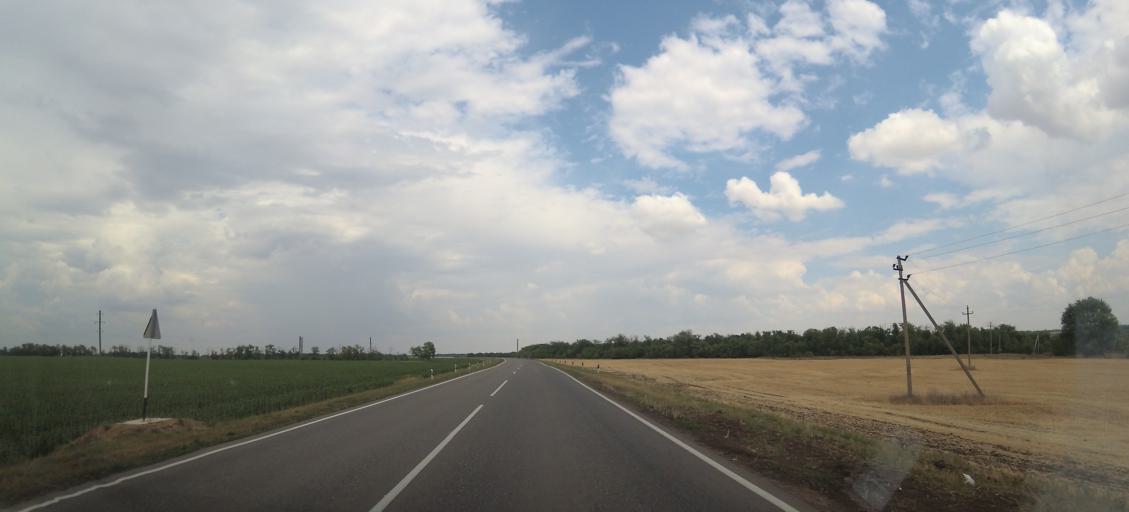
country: RU
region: Rostov
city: Krasnaya Polyana
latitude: 46.2514
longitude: 41.3374
